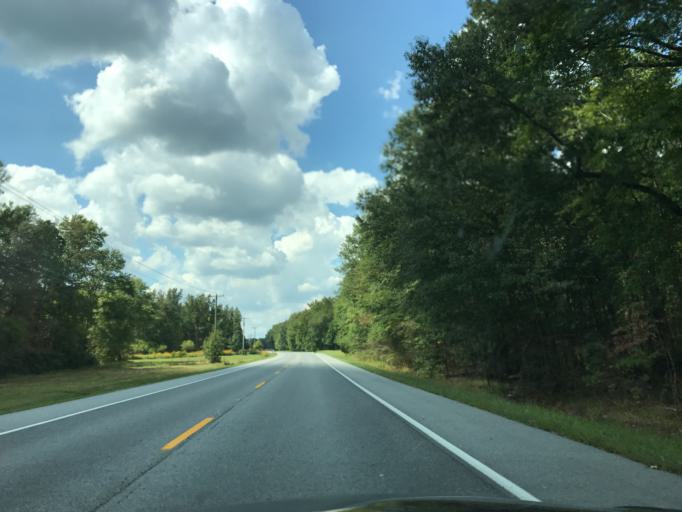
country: US
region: Maryland
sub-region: Caroline County
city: Greensboro
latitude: 39.1445
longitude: -75.8237
